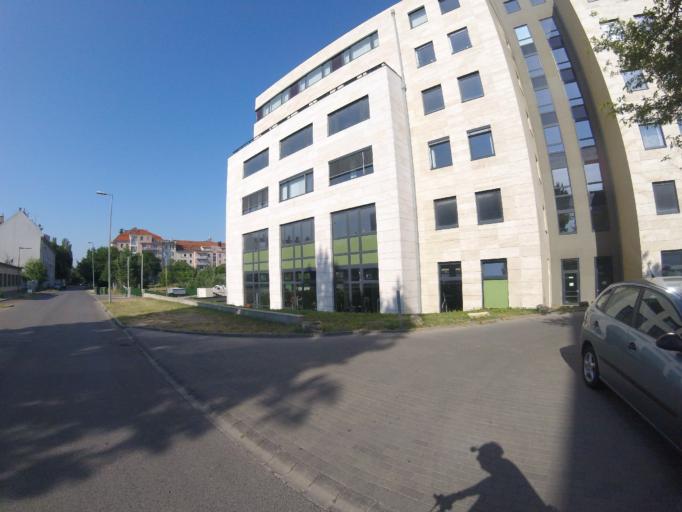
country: HU
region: Budapest
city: Budapest IV. keruelet
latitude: 47.5539
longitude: 19.0807
